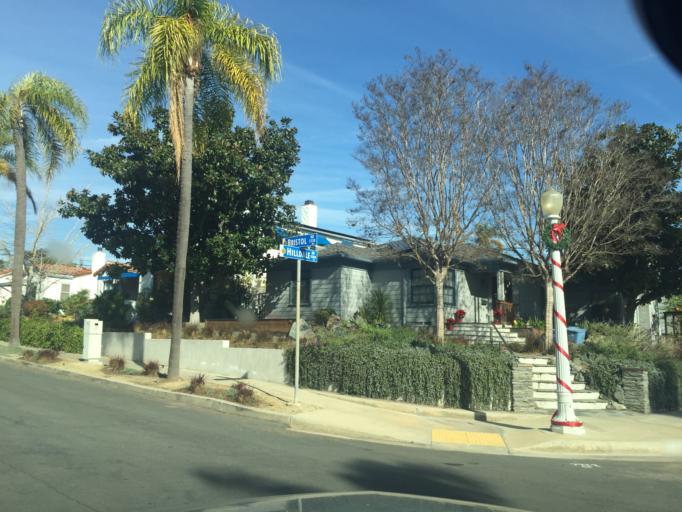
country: US
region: California
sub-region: San Diego County
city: Lemon Grove
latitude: 32.7707
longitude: -117.1022
